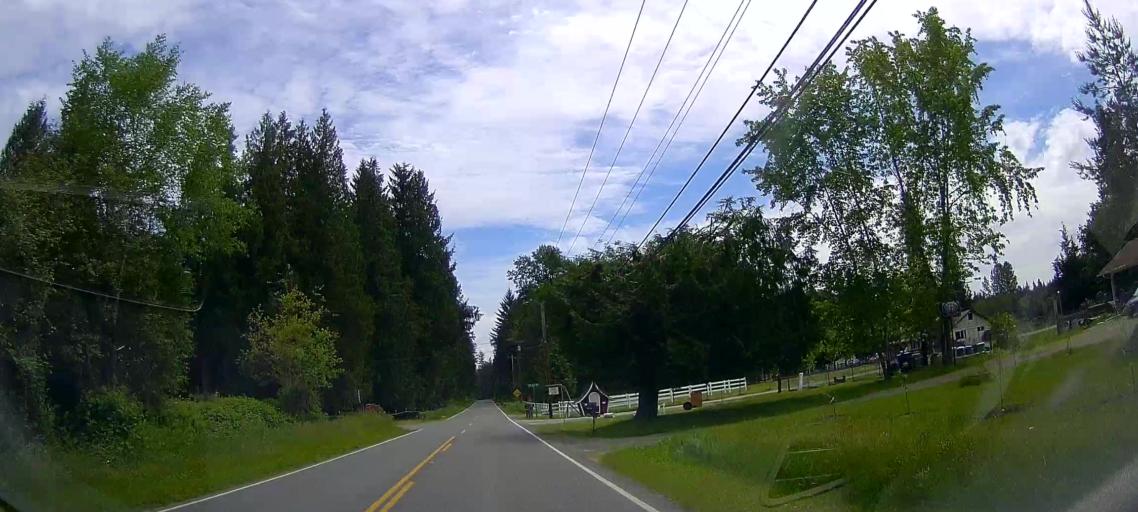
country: US
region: Washington
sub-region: Snohomish County
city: Bryant
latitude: 48.2388
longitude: -122.1778
